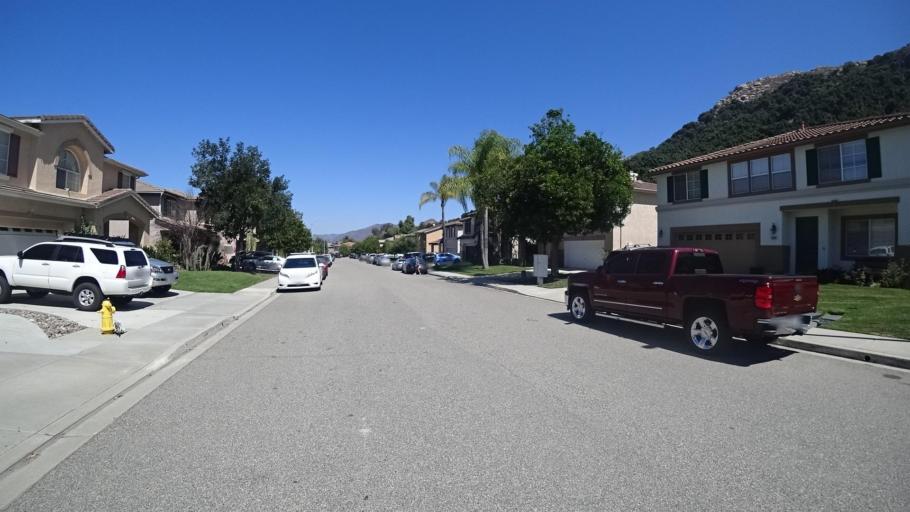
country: US
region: California
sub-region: San Diego County
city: Bonsall
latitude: 33.3193
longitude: -117.1478
